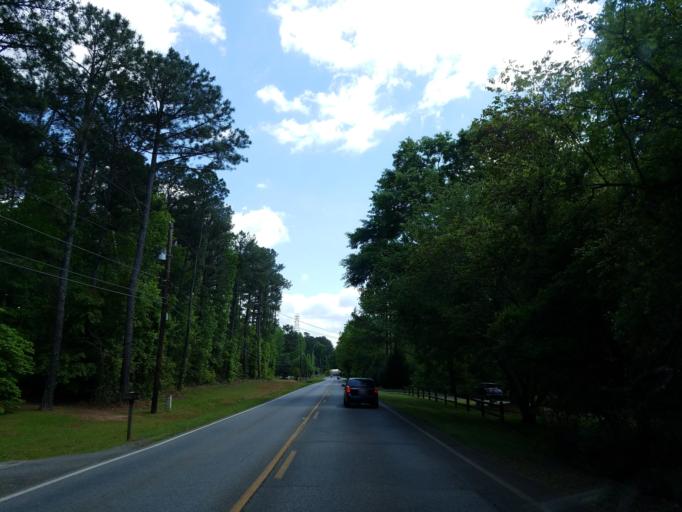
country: US
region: Georgia
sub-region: Monroe County
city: Forsyth
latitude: 33.0614
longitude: -83.9523
